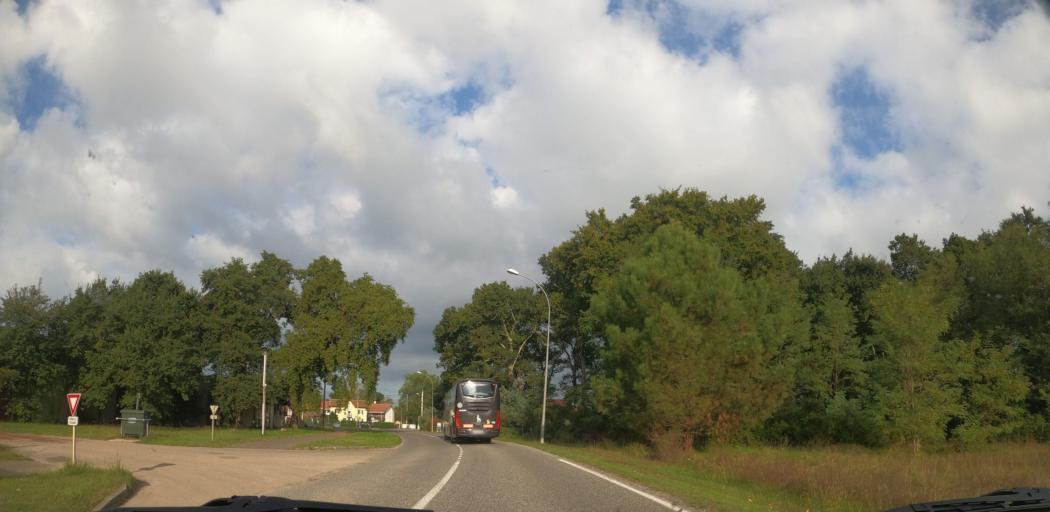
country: FR
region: Aquitaine
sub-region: Departement des Landes
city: Soustons
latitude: 43.7497
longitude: -1.3202
